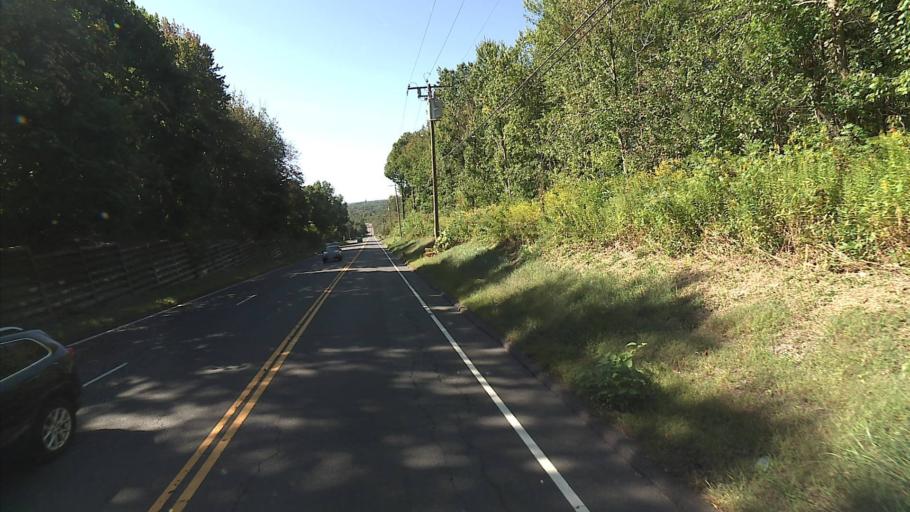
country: US
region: Connecticut
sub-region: New Haven County
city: Wolcott
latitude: 41.6151
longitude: -72.9790
